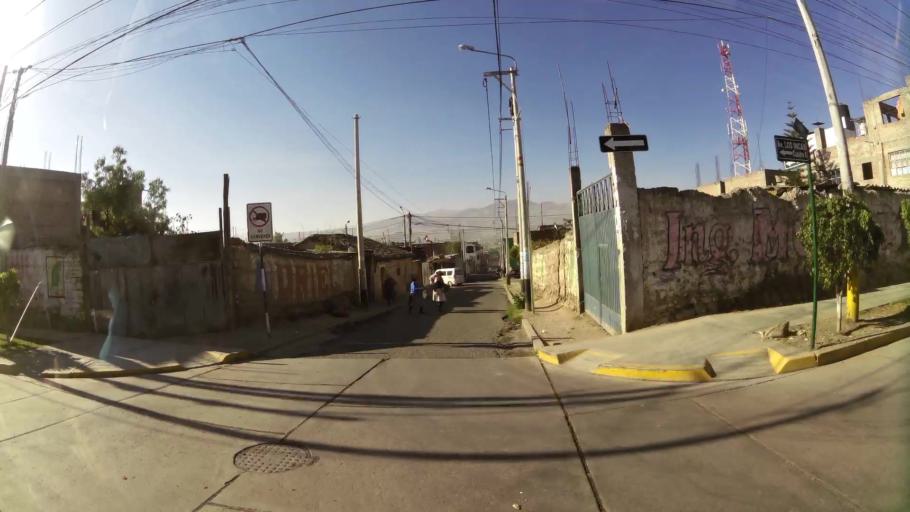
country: PE
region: Ayacucho
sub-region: Provincia de Huamanga
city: Ayacucho
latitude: -13.1513
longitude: -74.2134
